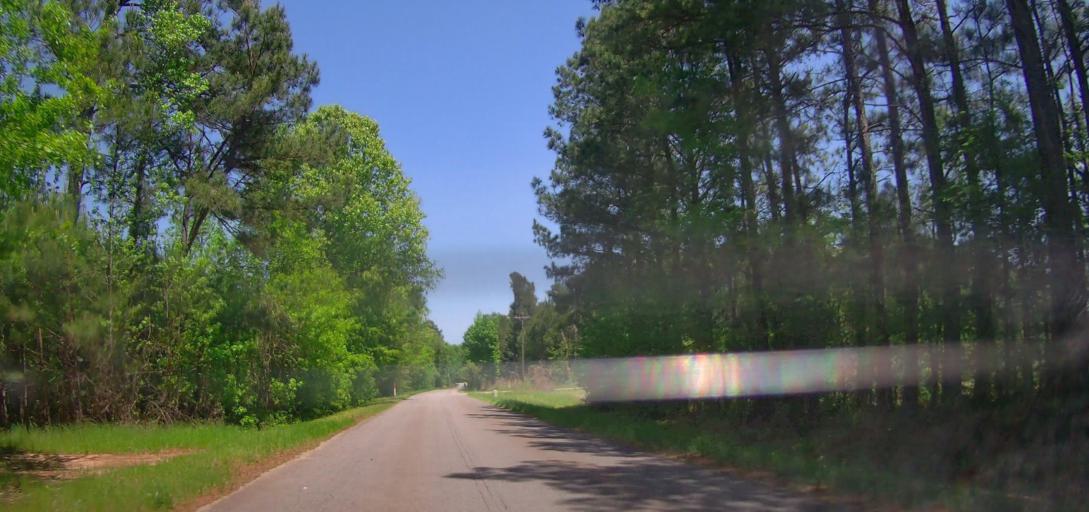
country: US
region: Georgia
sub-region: Jasper County
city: Monticello
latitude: 33.3243
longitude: -83.7100
